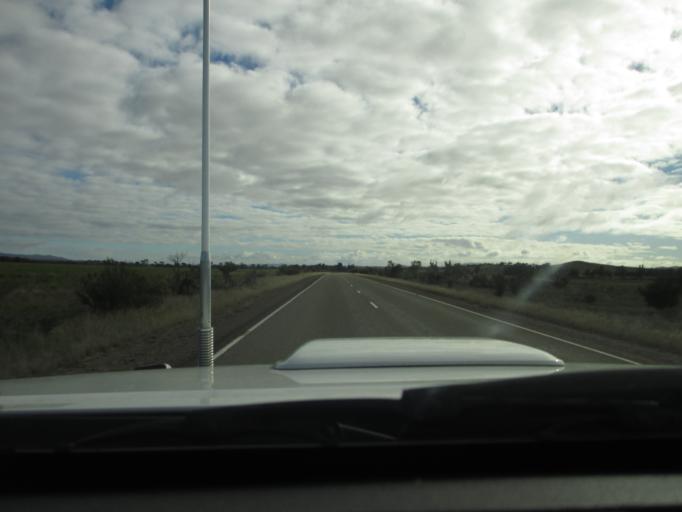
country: AU
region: South Australia
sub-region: Flinders Ranges
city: Quorn
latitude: -32.4940
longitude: 138.5470
